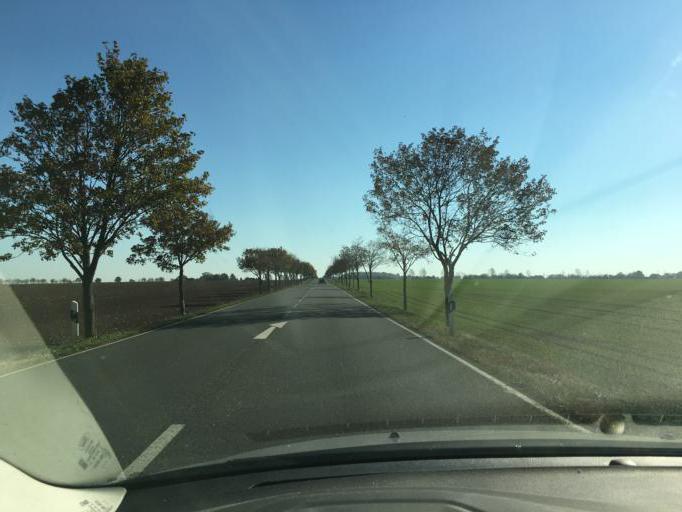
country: DE
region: Saxony-Anhalt
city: Wanzleben
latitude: 52.0480
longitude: 11.4563
